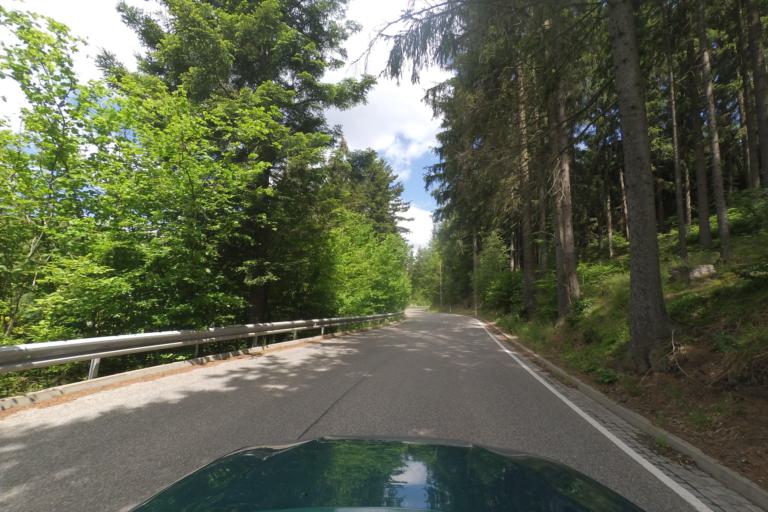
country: PL
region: Lower Silesian Voivodeship
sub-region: Powiat klodzki
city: Lewin Klodzki
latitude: 50.3499
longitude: 16.2390
